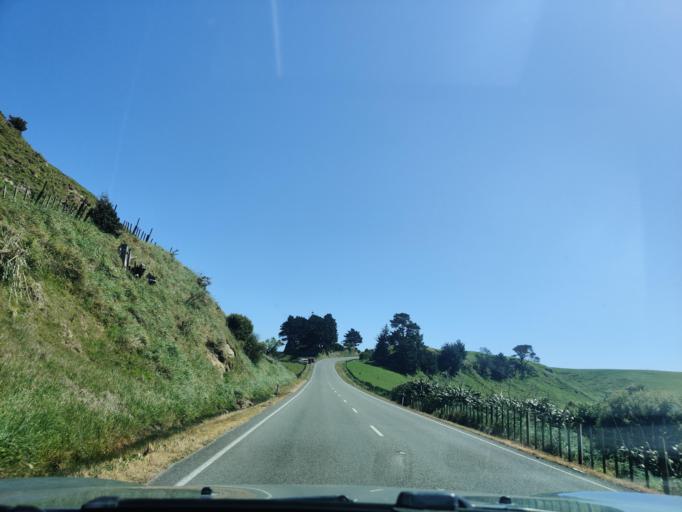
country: NZ
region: Taranaki
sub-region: South Taranaki District
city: Patea
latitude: -39.7571
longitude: 174.5418
